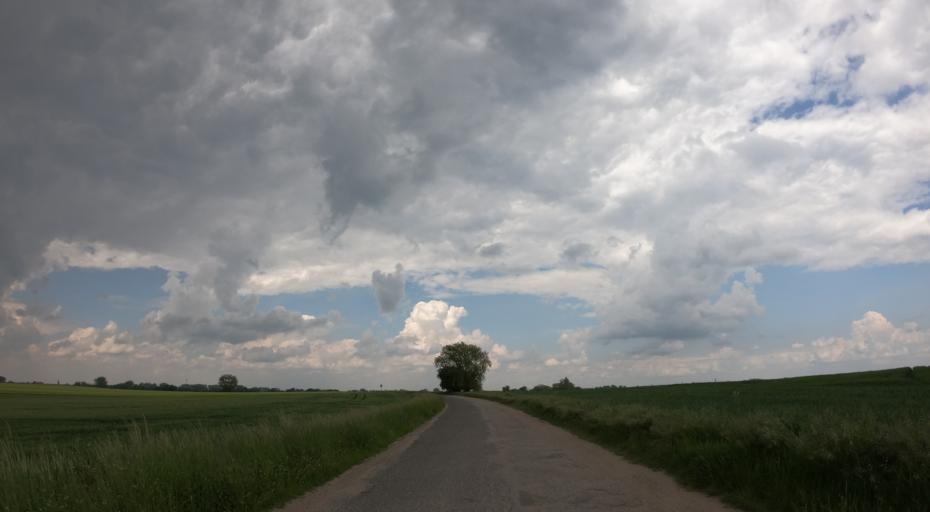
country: PL
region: West Pomeranian Voivodeship
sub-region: Powiat pyrzycki
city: Kozielice
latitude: 53.1604
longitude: 14.8004
